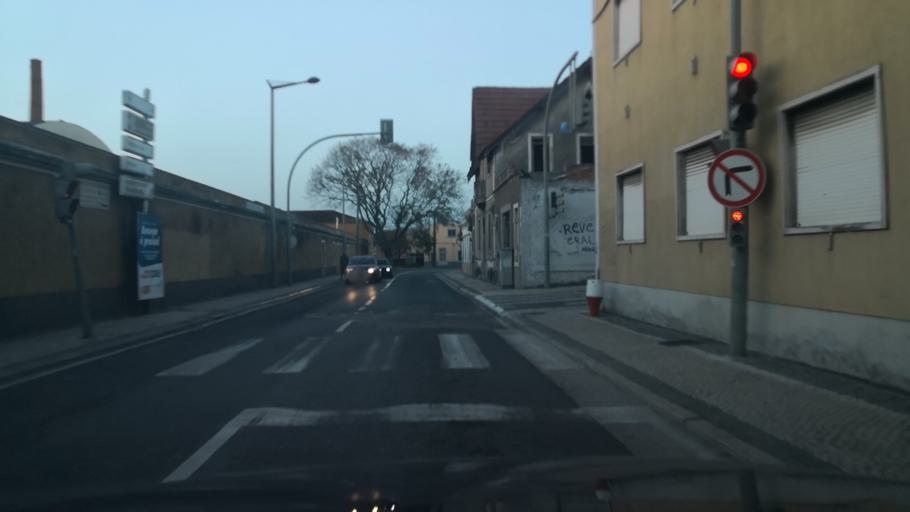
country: PT
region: Leiria
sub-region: Marinha Grande
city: Marinha Grande
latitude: 39.7505
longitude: -8.9334
